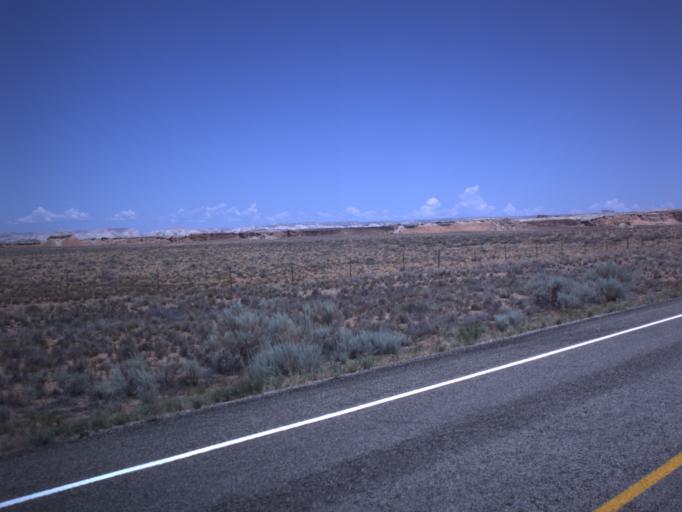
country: US
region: Utah
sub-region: Emery County
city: Ferron
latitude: 38.4167
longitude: -110.6935
